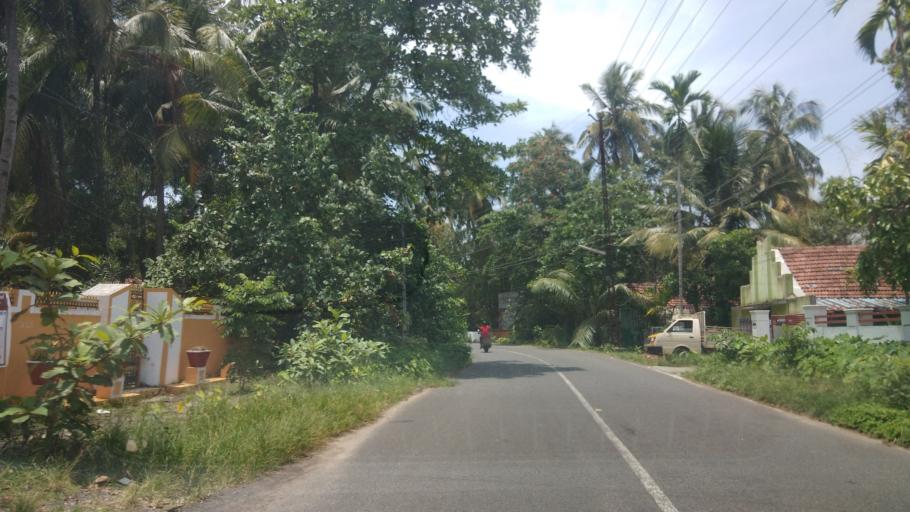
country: IN
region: Kerala
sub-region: Alappuzha
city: Arukutti
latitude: 9.8532
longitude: 76.2662
